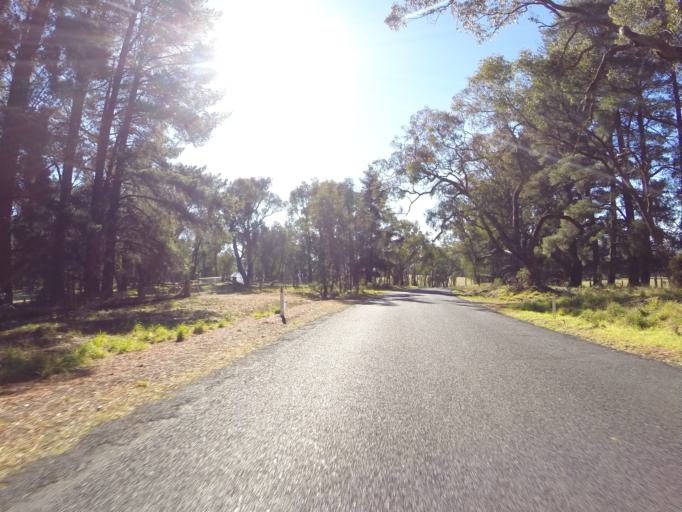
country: AU
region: New South Wales
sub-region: Oberon
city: Oberon
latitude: -33.5746
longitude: 149.8631
